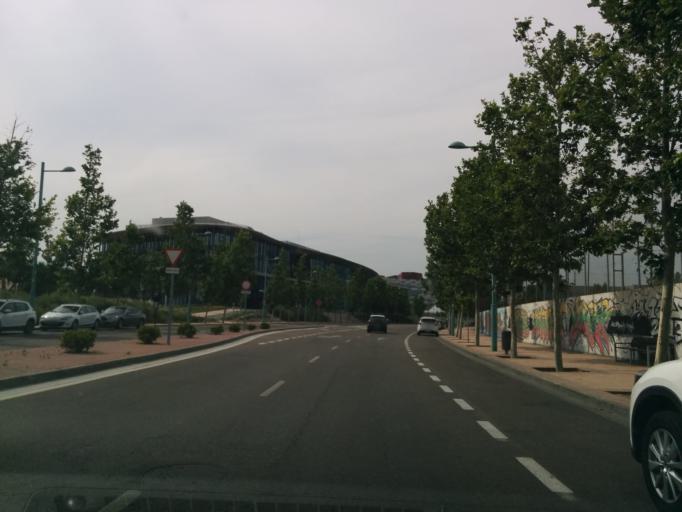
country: ES
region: Aragon
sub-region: Provincia de Zaragoza
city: Almozara
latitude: 41.6674
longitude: -0.8954
